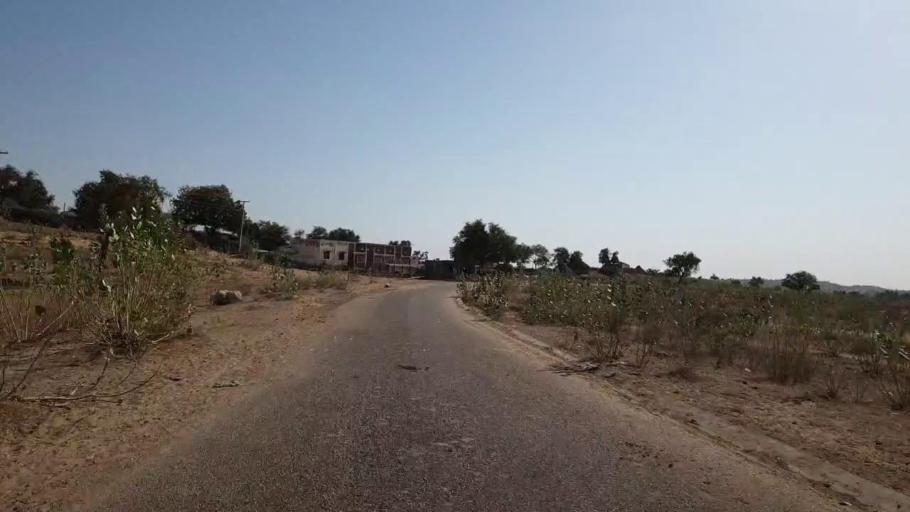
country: PK
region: Sindh
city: Umarkot
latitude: 25.1153
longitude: 70.0421
